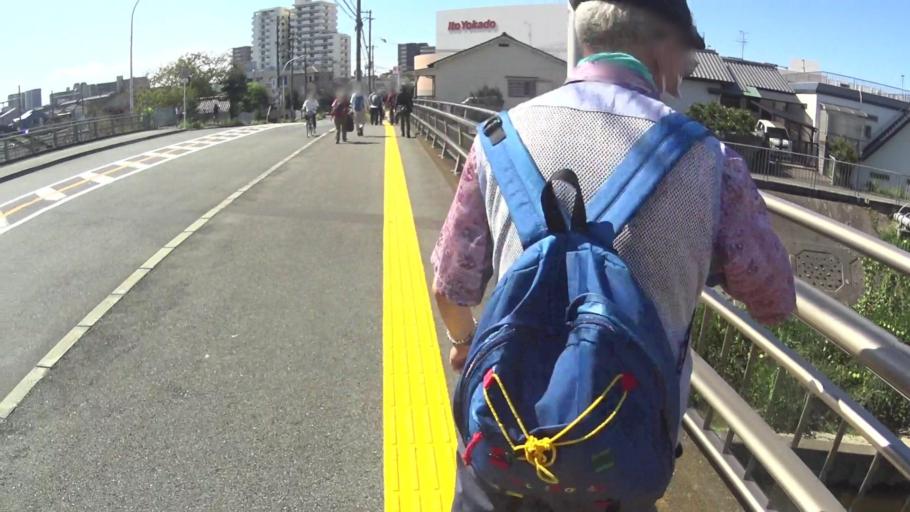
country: JP
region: Osaka
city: Sakai
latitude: 34.5418
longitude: 135.4665
